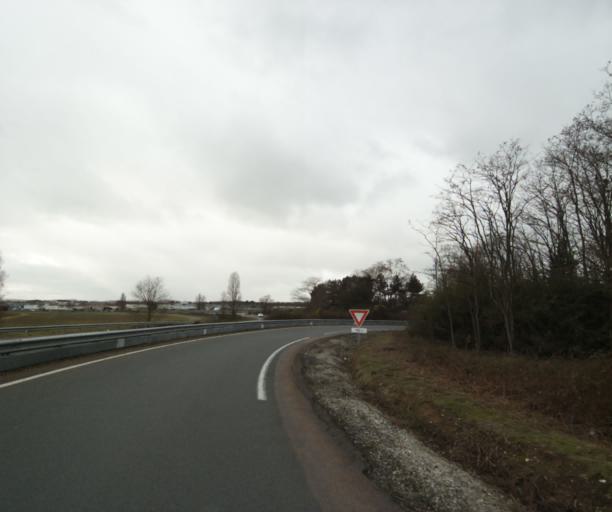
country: FR
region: Pays de la Loire
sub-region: Departement de la Sarthe
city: Arnage
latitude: 47.9547
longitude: 0.1998
